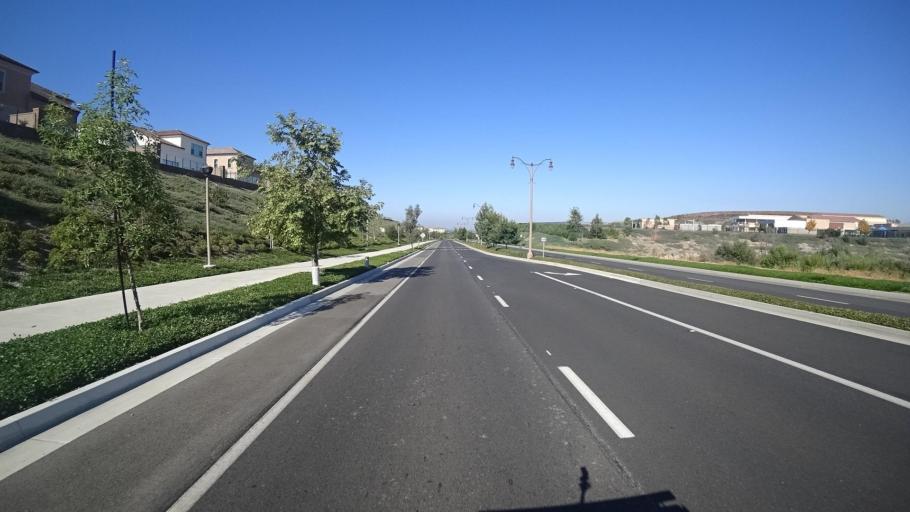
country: US
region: California
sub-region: Orange County
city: Foothill Ranch
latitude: 33.6945
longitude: -117.7021
